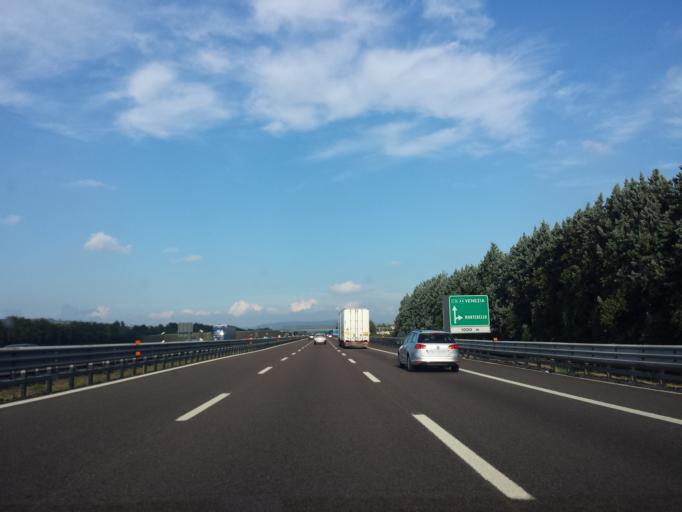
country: IT
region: Veneto
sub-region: Provincia di Verona
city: Locara
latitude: 45.4294
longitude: 11.3399
